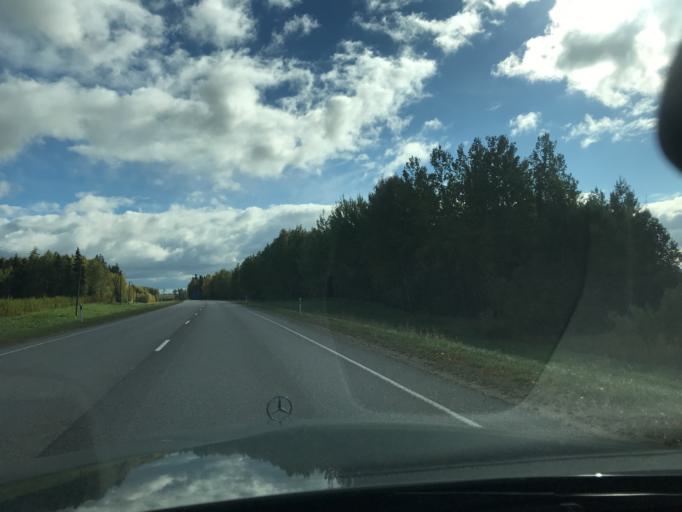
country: EE
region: Vorumaa
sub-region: Voru linn
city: Voru
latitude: 57.8531
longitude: 27.0278
